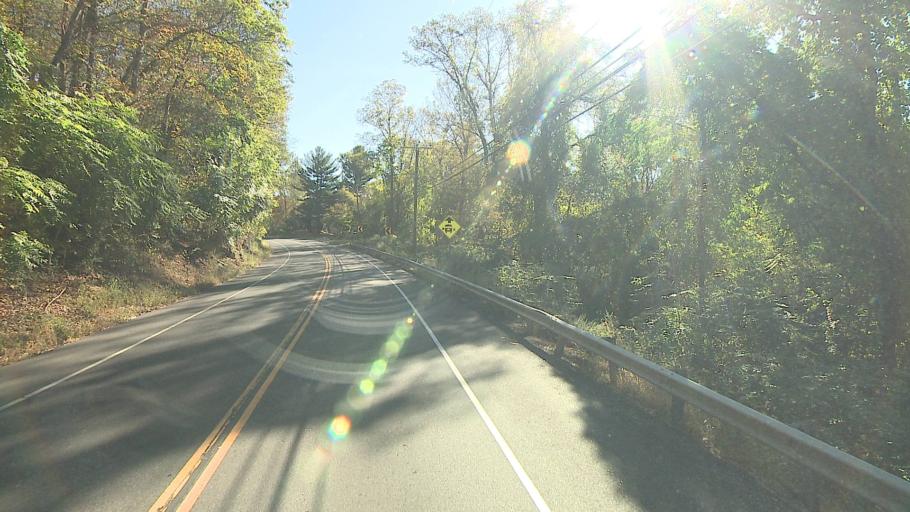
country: US
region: Connecticut
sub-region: Middlesex County
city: East Hampton
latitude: 41.5619
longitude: -72.5519
